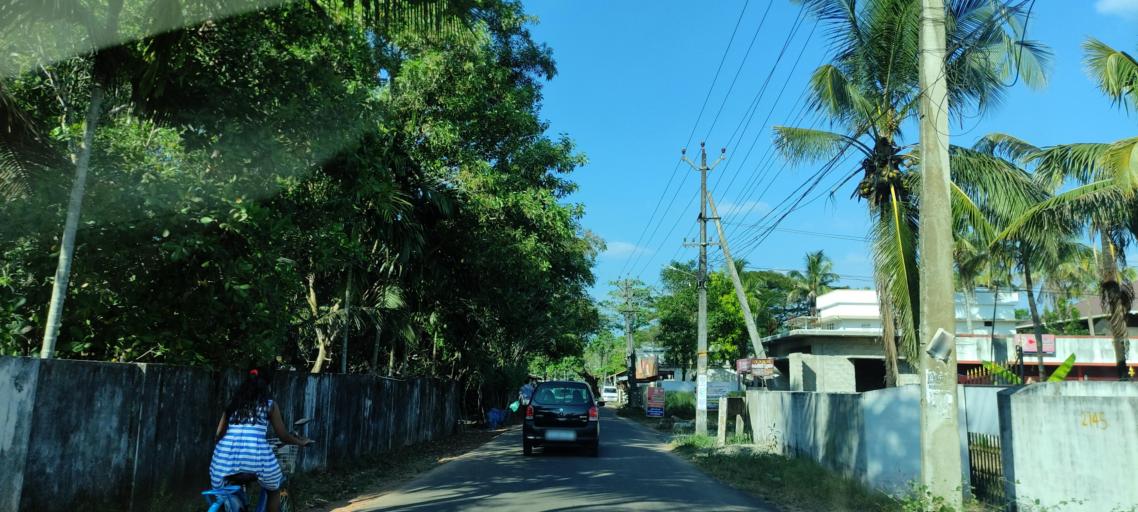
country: IN
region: Kerala
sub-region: Alappuzha
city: Shertallai
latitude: 9.6226
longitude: 76.3427
